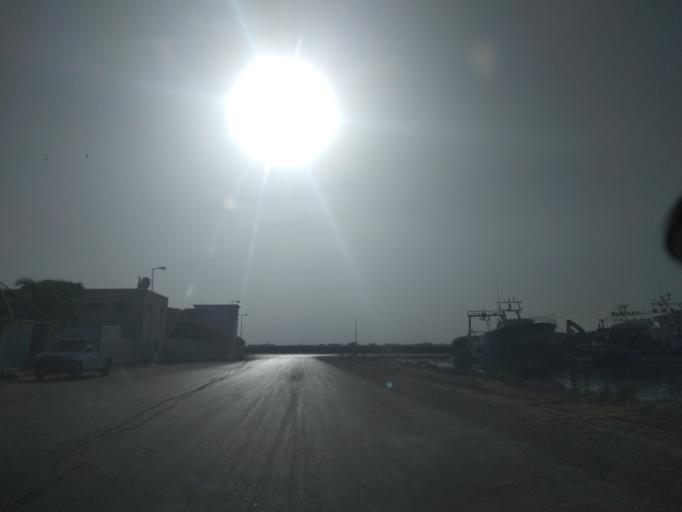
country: TN
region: Safaqis
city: Sfax
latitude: 34.7156
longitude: 10.7623
